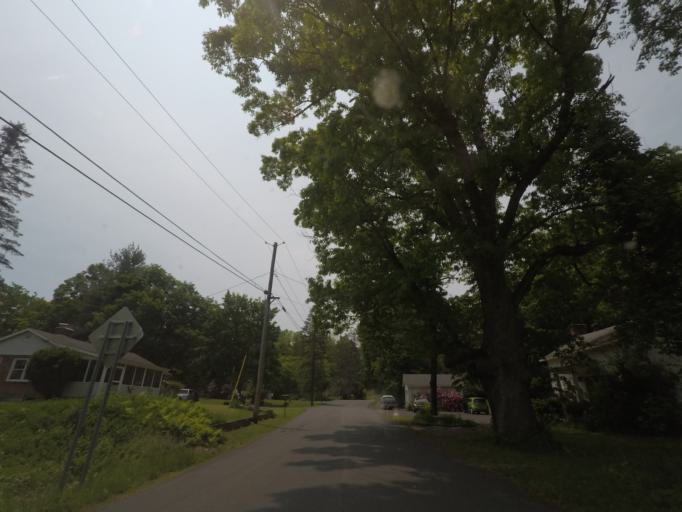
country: US
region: New York
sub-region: Rensselaer County
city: East Greenbush
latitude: 42.5493
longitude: -73.6909
